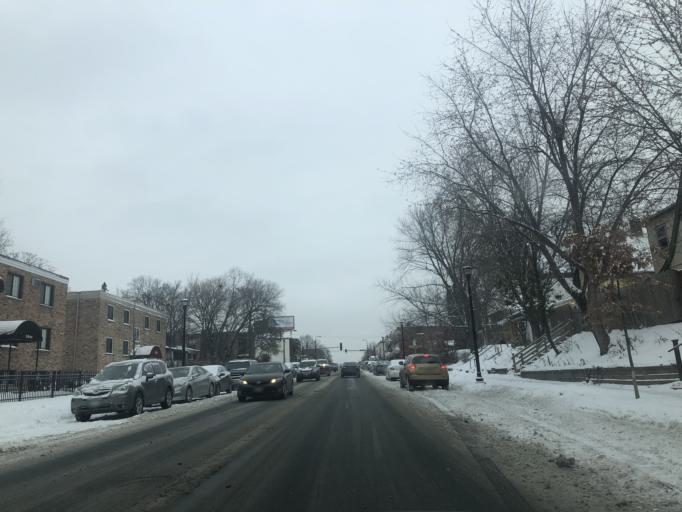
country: US
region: Minnesota
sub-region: Hennepin County
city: Richfield
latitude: 44.9325
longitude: -93.2779
